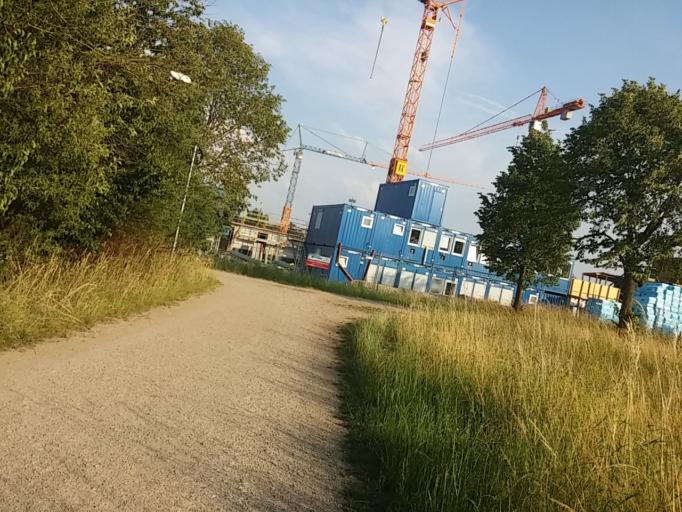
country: DE
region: Bavaria
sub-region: Upper Bavaria
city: Vaterstetten
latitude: 48.1126
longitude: 11.7689
